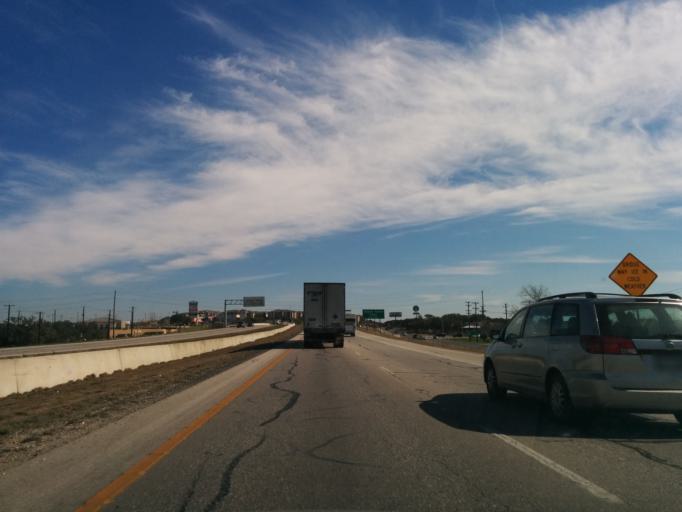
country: US
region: Texas
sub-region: Bexar County
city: Shavano Park
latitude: 29.5983
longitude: -98.5663
